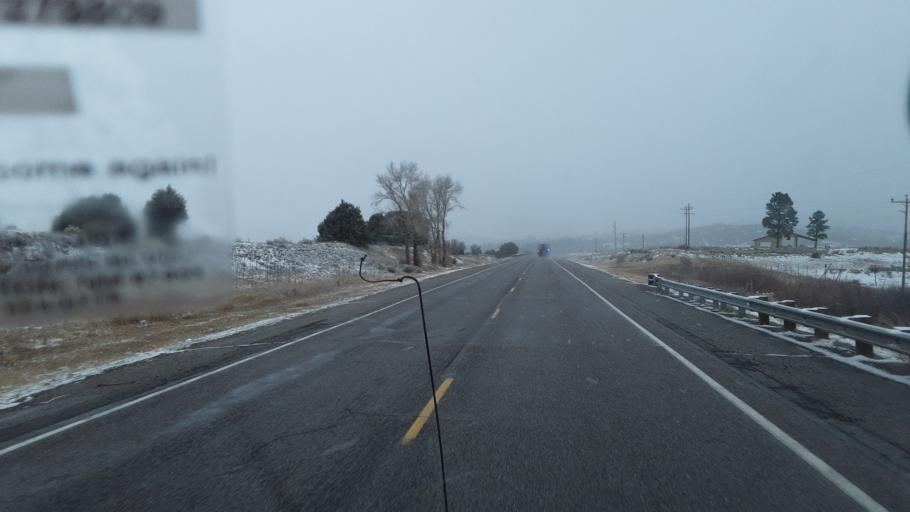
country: US
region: New Mexico
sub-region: Rio Arriba County
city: Tierra Amarilla
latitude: 36.7766
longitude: -106.5559
